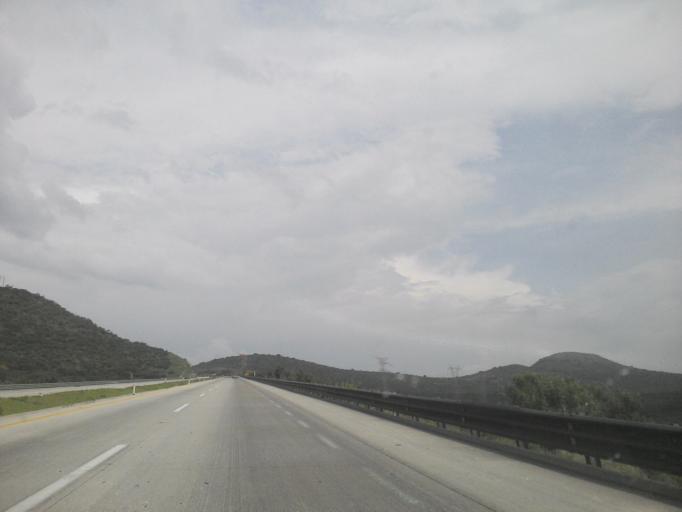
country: MX
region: Mexico
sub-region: Apaxco
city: Colonia Juarez
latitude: 20.0259
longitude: -99.1707
